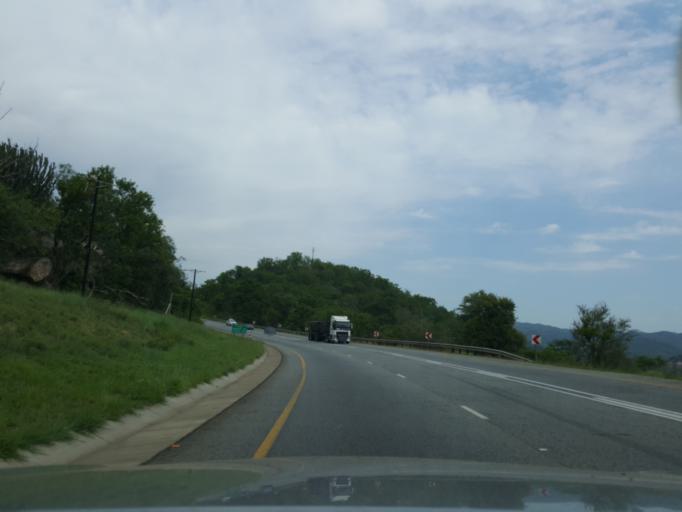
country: ZA
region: Mpumalanga
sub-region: Ehlanzeni District
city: Nelspruit
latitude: -25.4941
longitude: 31.1619
